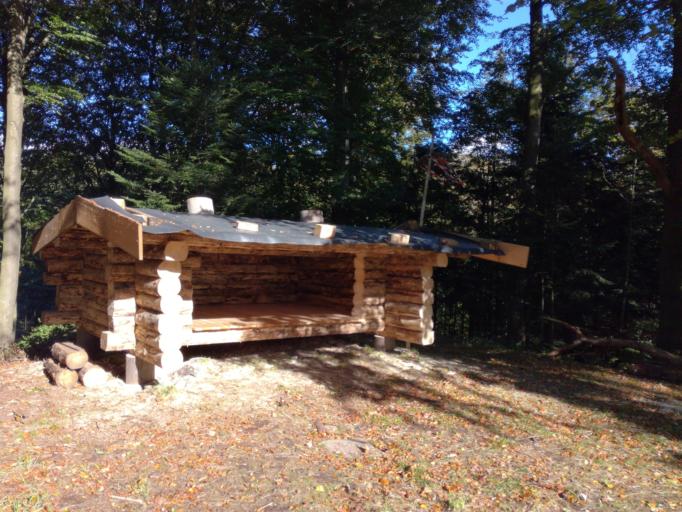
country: DK
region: South Denmark
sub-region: Vejle Kommune
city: Brejning
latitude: 55.6728
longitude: 9.6761
